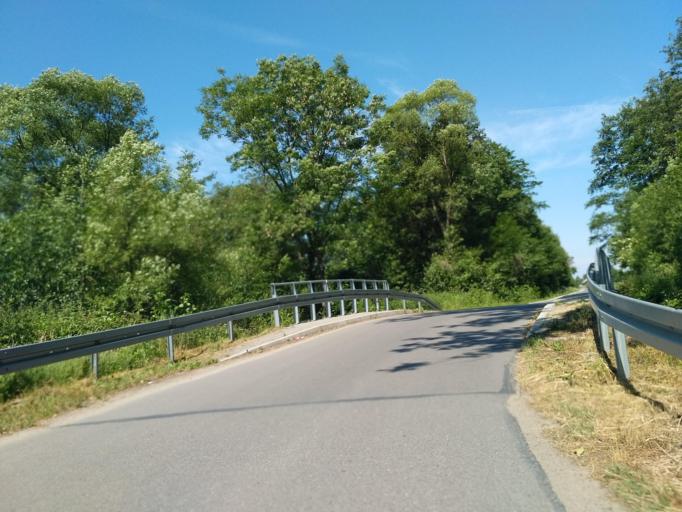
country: PL
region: Subcarpathian Voivodeship
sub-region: Powiat krosnienski
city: Korczyna
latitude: 49.7169
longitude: 21.7828
